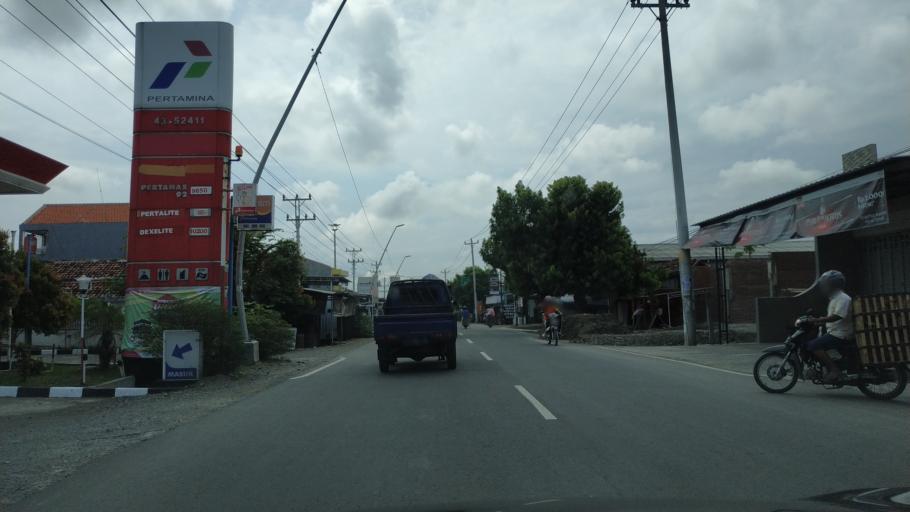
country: ID
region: Central Java
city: Tegal
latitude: -6.8985
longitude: 109.1256
